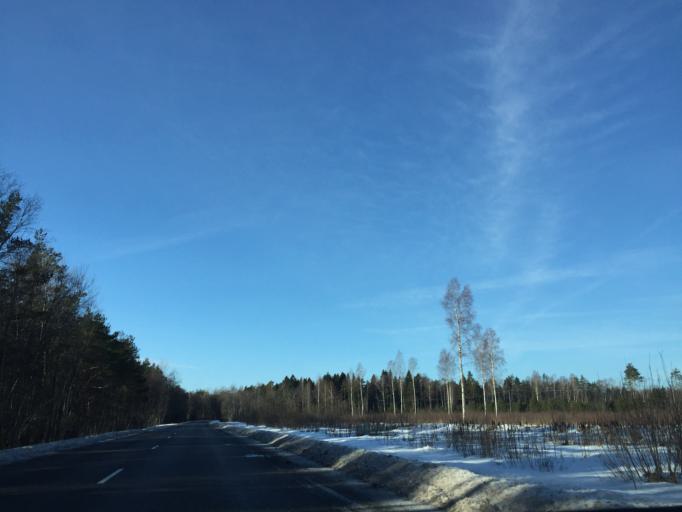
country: EE
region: Laeaene
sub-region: Lihula vald
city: Lihula
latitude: 58.5513
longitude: 23.8658
